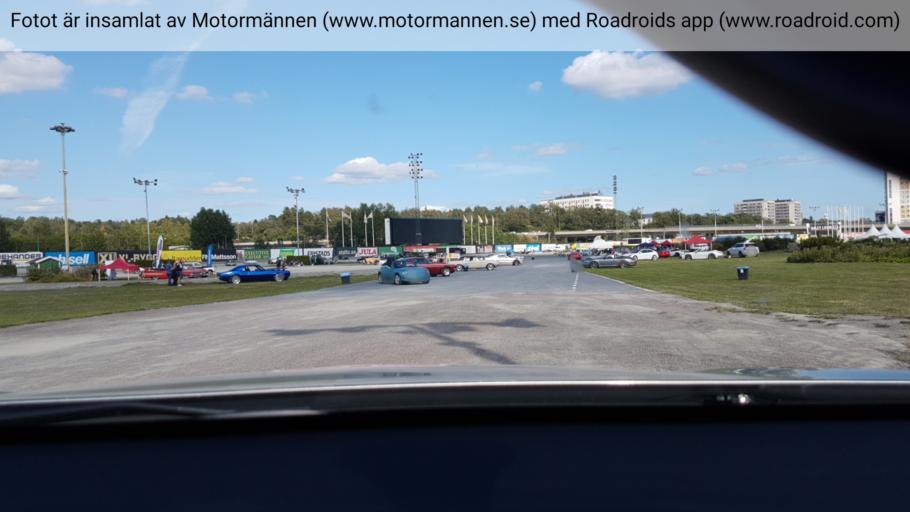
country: SE
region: Stockholm
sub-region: Stockholms Kommun
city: Bromma
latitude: 59.3678
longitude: 17.9374
